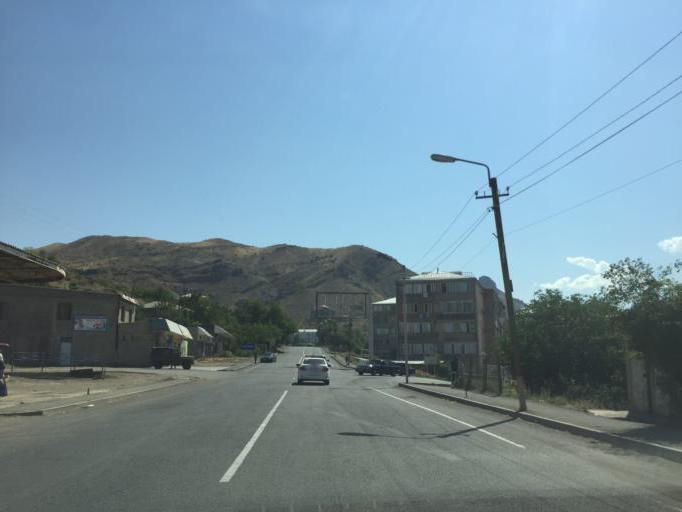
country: AM
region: Vayots' Dzori Marz
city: Vayk'
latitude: 39.6953
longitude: 45.4543
